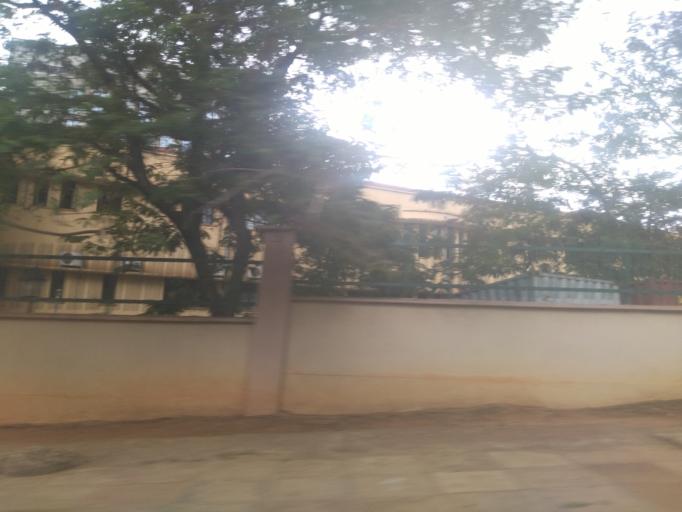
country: UG
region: Central Region
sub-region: Kampala District
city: Kampala
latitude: 0.3168
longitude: 32.5863
